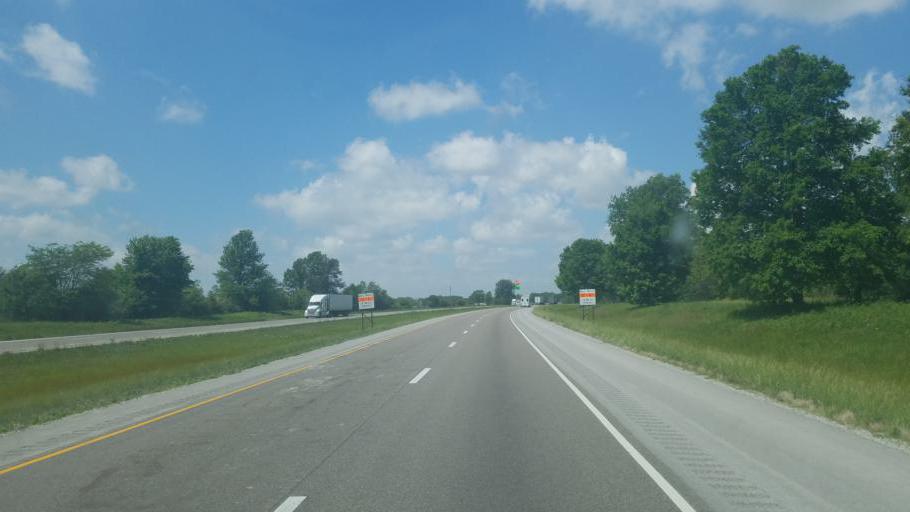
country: US
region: Illinois
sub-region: Cumberland County
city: Greenup
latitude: 39.2572
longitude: -88.1421
